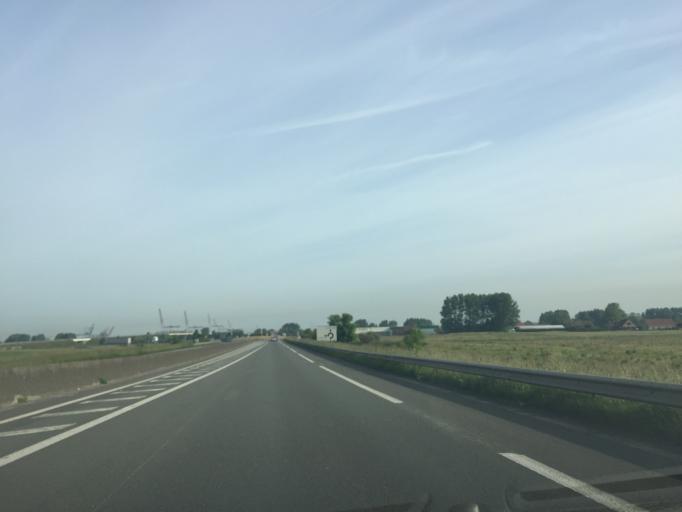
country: FR
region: Nord-Pas-de-Calais
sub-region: Departement du Nord
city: Loon-Plage
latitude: 50.9889
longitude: 2.2054
